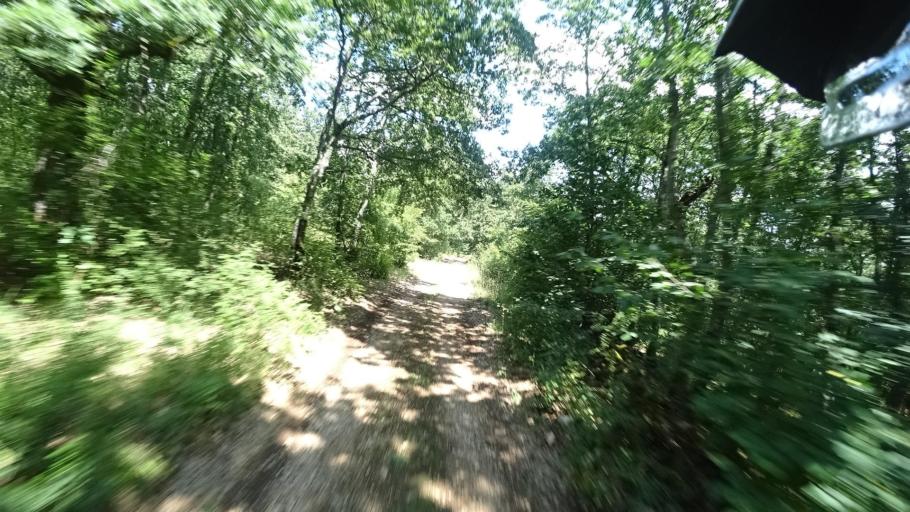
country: HR
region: Licko-Senjska
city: Gospic
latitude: 44.6268
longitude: 15.6161
